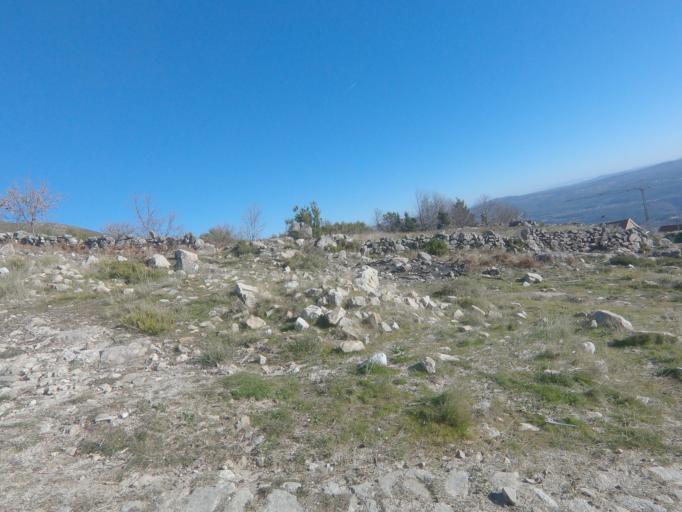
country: PT
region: Vila Real
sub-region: Vila Real
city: Vila Real
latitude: 41.3491
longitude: -7.7641
